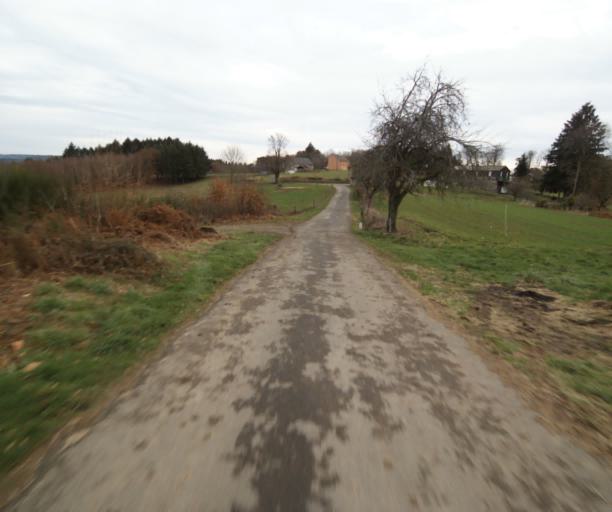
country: FR
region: Limousin
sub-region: Departement de la Correze
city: Cornil
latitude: 45.2268
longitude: 1.6755
